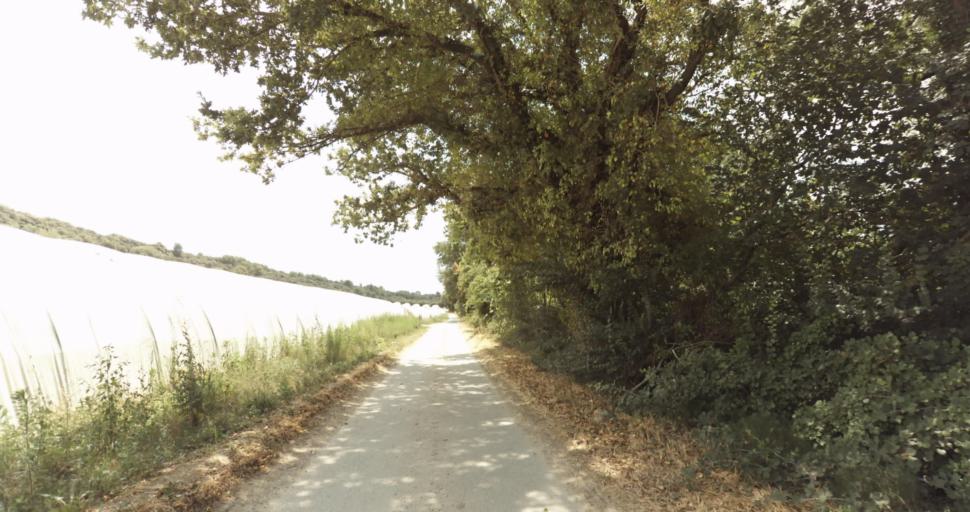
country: FR
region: Provence-Alpes-Cote d'Azur
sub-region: Departement du Vaucluse
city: Loriol-du-Comtat
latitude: 44.0642
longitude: 4.9913
